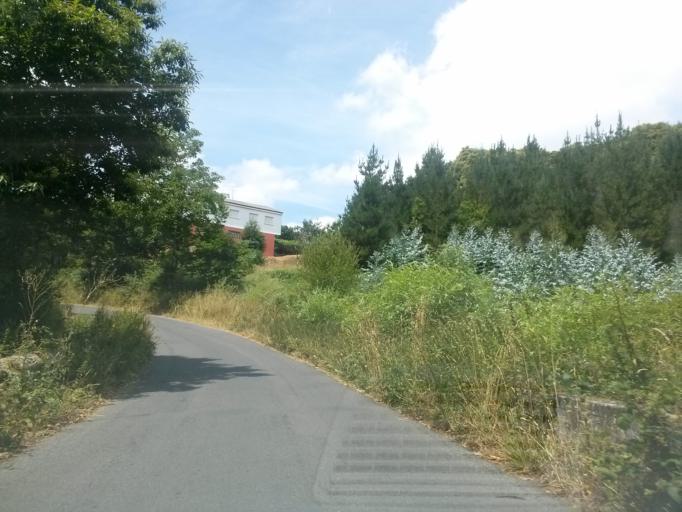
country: ES
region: Galicia
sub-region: Provincia de Lugo
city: Lugo
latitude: 43.0355
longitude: -7.5874
